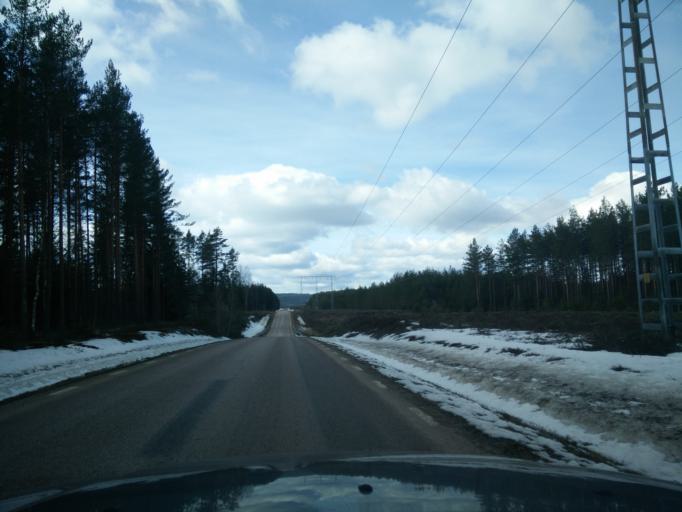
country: SE
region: Vaermland
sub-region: Hagfors Kommun
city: Hagfors
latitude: 60.0369
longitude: 13.5524
